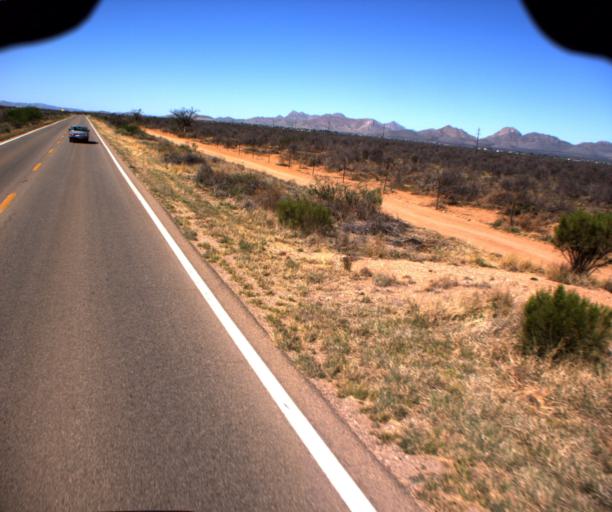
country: US
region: Arizona
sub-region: Cochise County
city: Huachuca City
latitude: 31.6989
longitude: -110.3007
